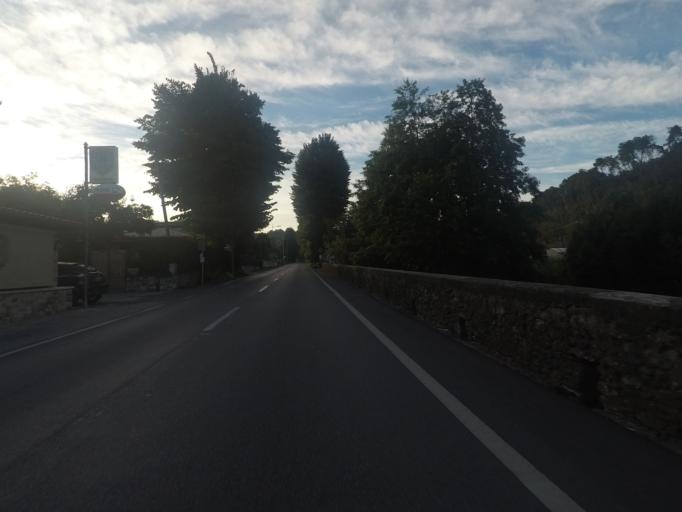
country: IT
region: Tuscany
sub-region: Provincia di Lucca
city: Corsanico-Bargecchia
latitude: 43.9235
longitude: 10.3266
